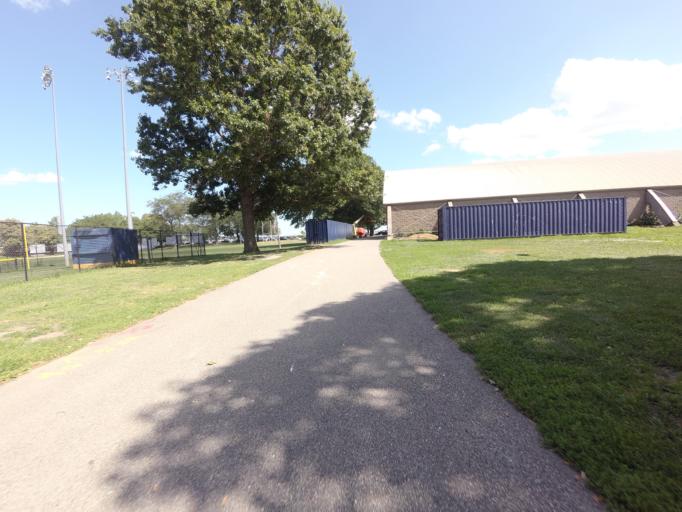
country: US
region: Massachusetts
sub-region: Suffolk County
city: South Boston
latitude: 42.3375
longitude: -71.0243
